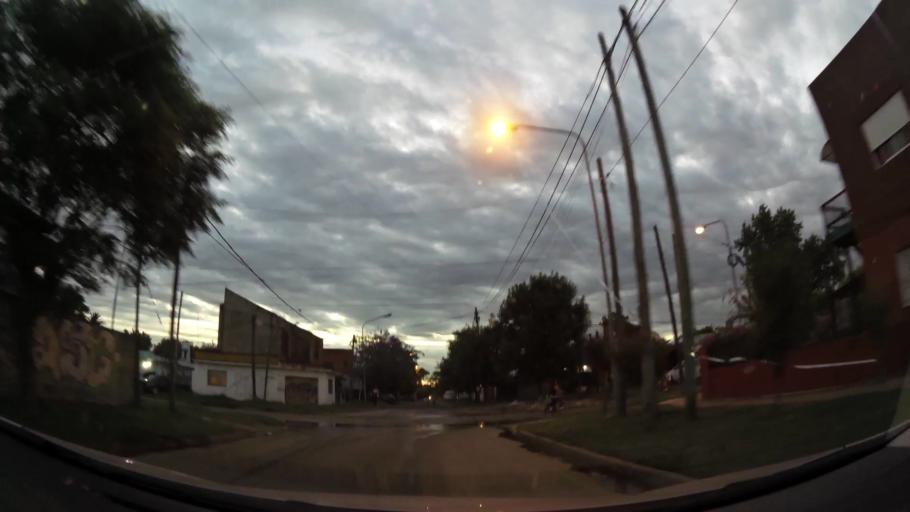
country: AR
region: Buenos Aires
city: Santa Catalina - Dique Lujan
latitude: -34.4149
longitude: -58.6880
